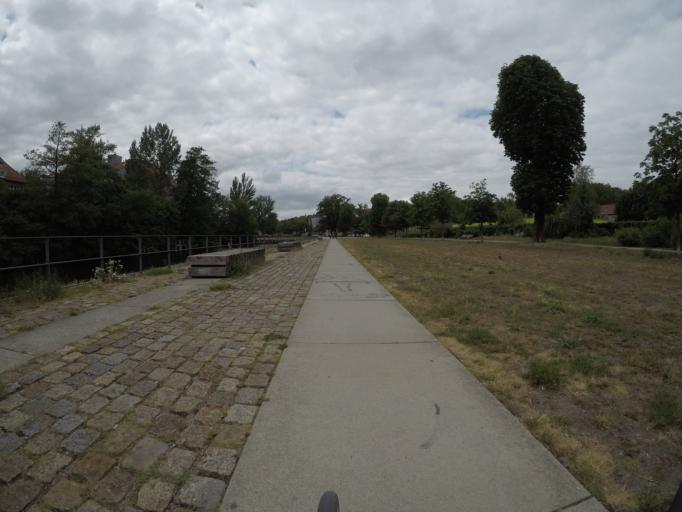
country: DE
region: Berlin
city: Hakenfelde
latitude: 52.5550
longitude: 13.2104
